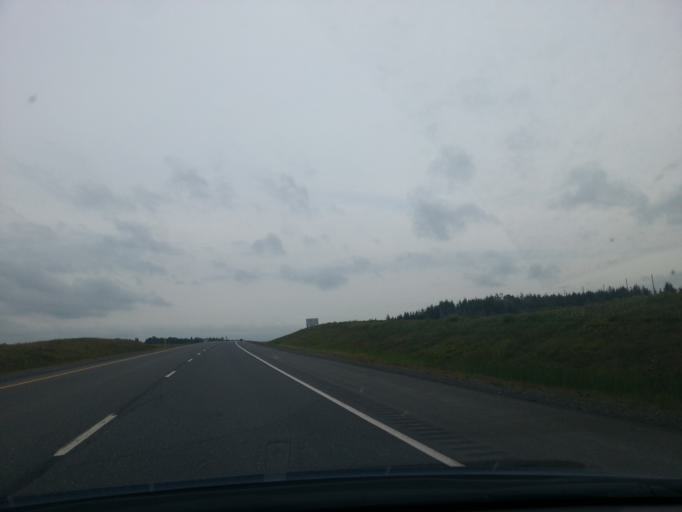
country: CA
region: New Brunswick
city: Florenceville-Bristol
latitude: 46.3307
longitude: -67.5993
